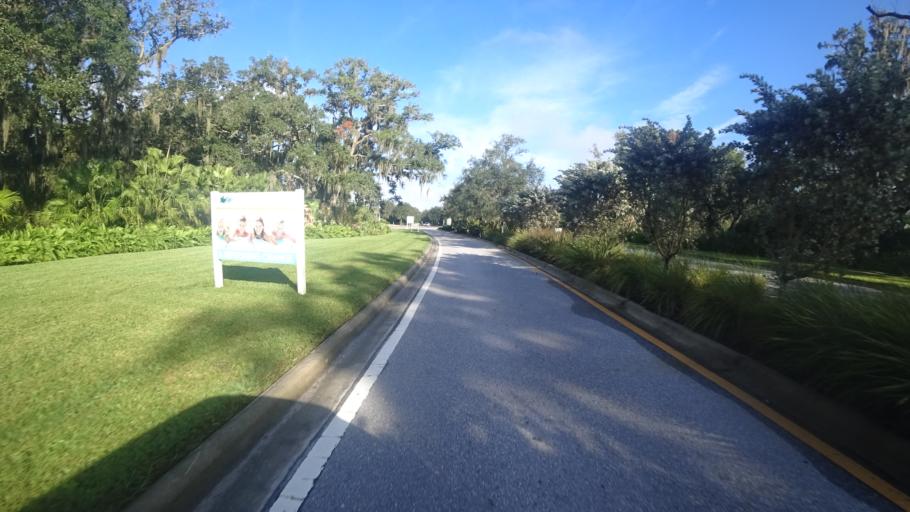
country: US
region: Florida
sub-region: Manatee County
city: Ellenton
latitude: 27.5542
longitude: -82.4530
